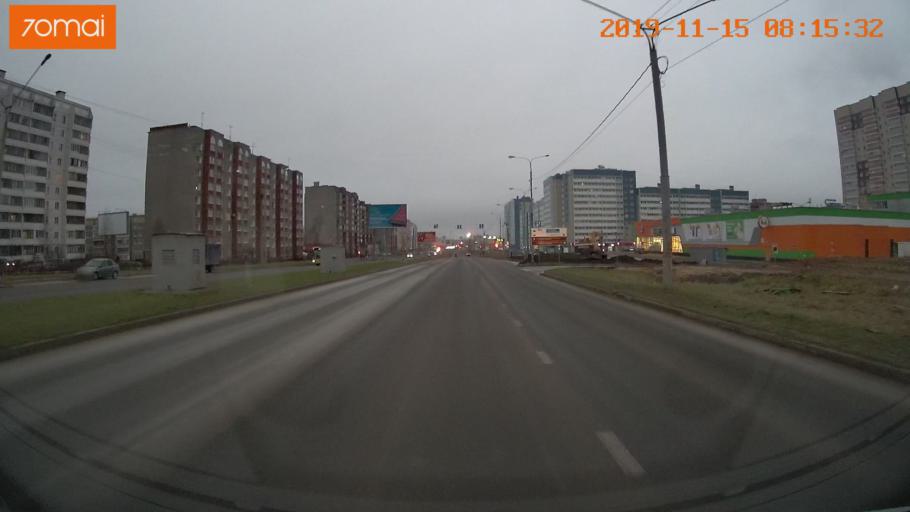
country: RU
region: Vologda
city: Cherepovets
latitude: 59.0832
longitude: 37.9217
